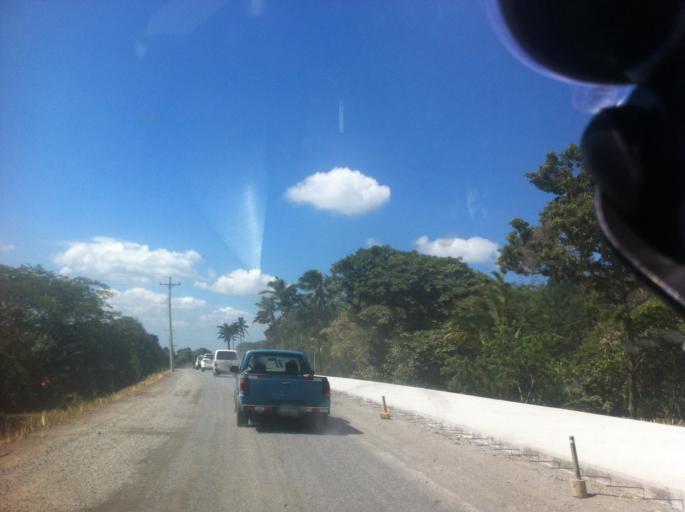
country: NI
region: Managua
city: Ciudad Sandino
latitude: 12.0832
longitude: -86.3813
